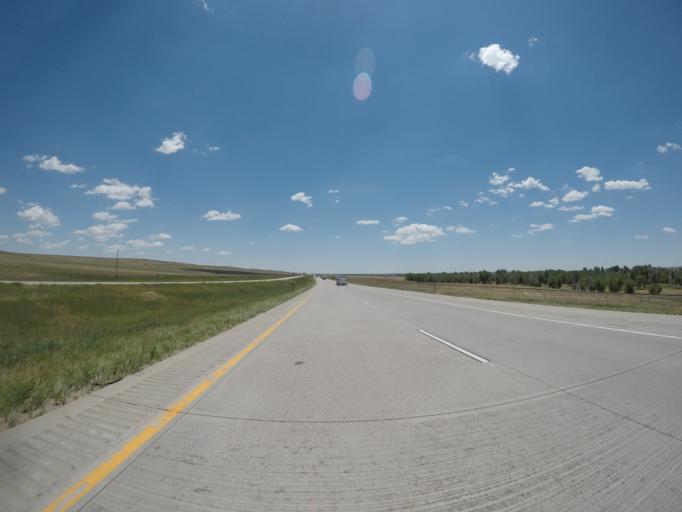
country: US
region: Colorado
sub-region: Lincoln County
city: Limon
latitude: 39.3023
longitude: -103.8147
